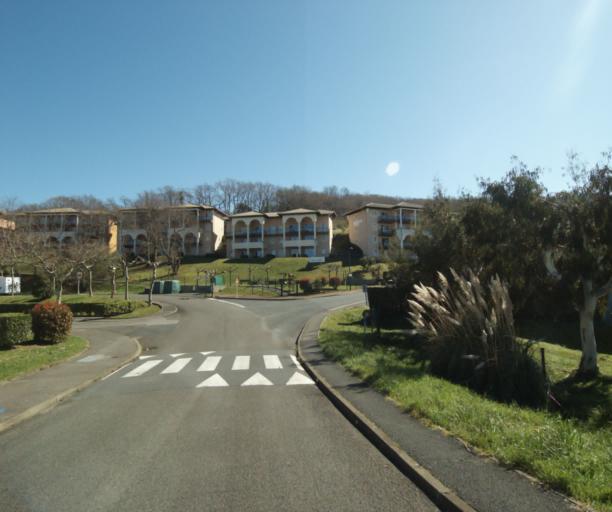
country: FR
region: Aquitaine
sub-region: Departement des Pyrenees-Atlantiques
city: Ciboure
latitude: 43.3860
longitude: -1.6873
